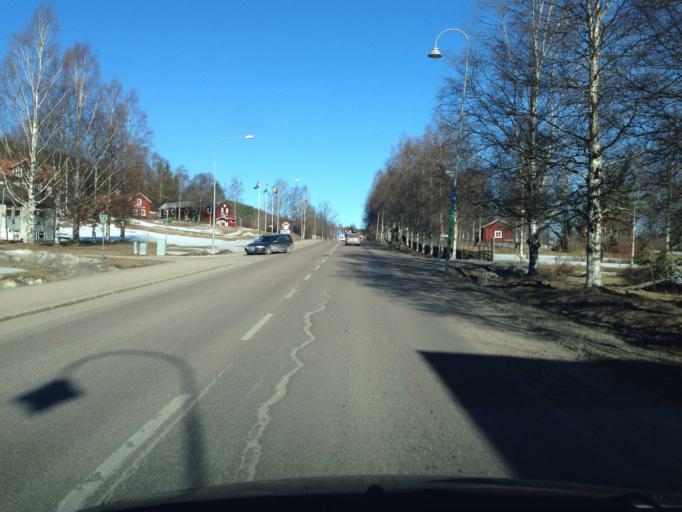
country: SE
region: Gaevleborg
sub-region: Ljusdals Kommun
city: Jaervsoe
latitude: 61.7192
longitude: 16.1697
